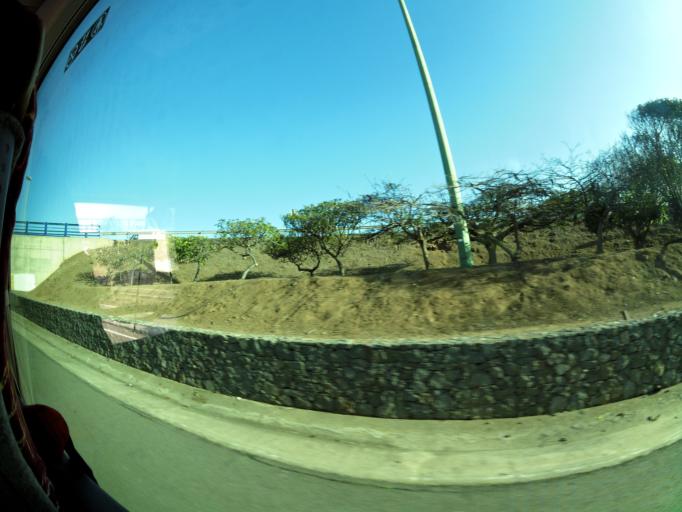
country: ES
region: Canary Islands
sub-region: Provincia de Las Palmas
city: Guia
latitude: 28.1431
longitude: -15.6380
